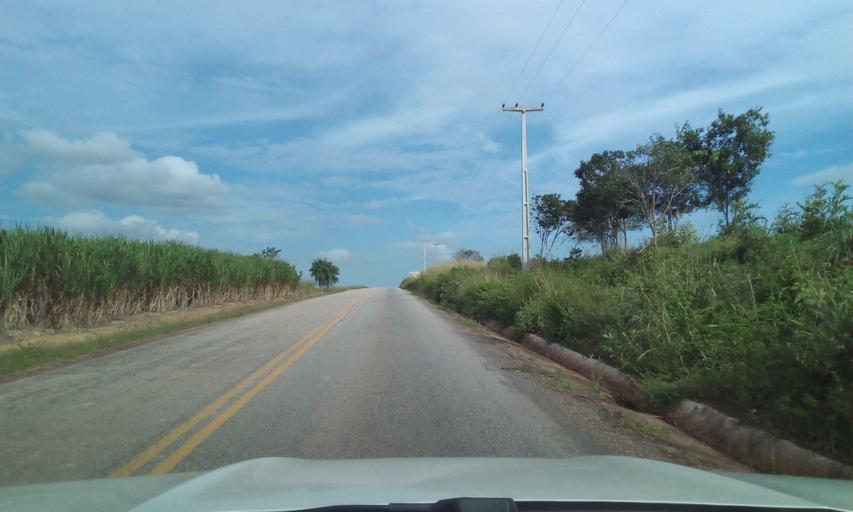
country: BR
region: Paraiba
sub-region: Santa Rita
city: Santa Rita
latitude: -6.9890
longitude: -34.9912
